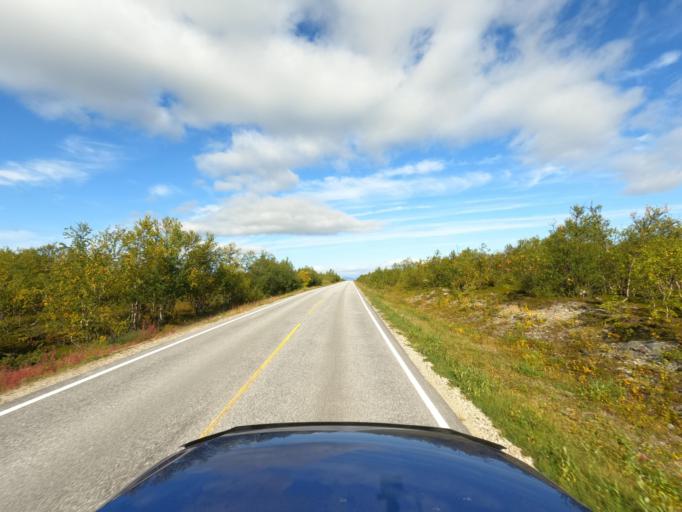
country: NO
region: Finnmark Fylke
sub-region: Karasjok
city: Karasjohka
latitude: 69.6166
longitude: 25.3007
